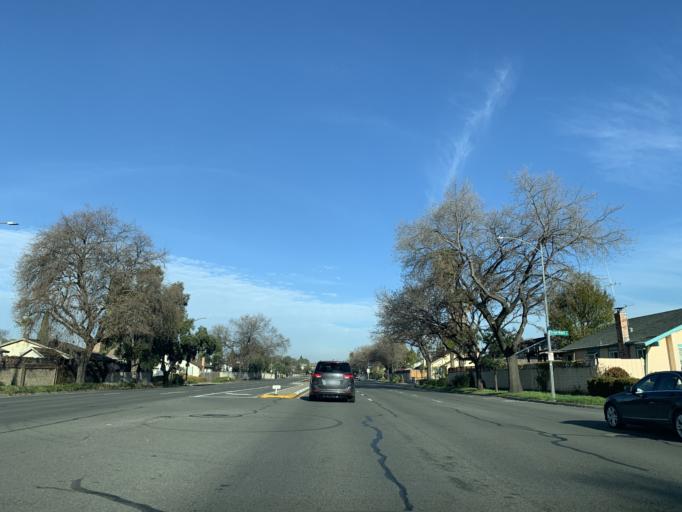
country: US
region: California
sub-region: Santa Clara County
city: Seven Trees
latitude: 37.2711
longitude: -121.8361
